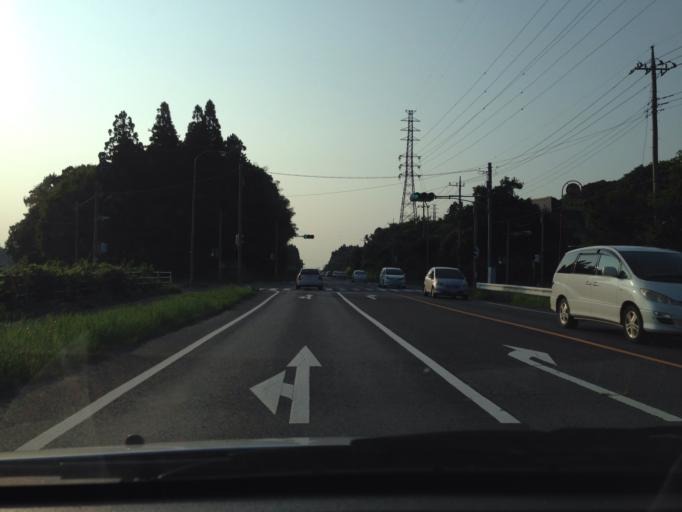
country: JP
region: Ibaraki
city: Ami
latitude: 36.0262
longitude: 140.2346
